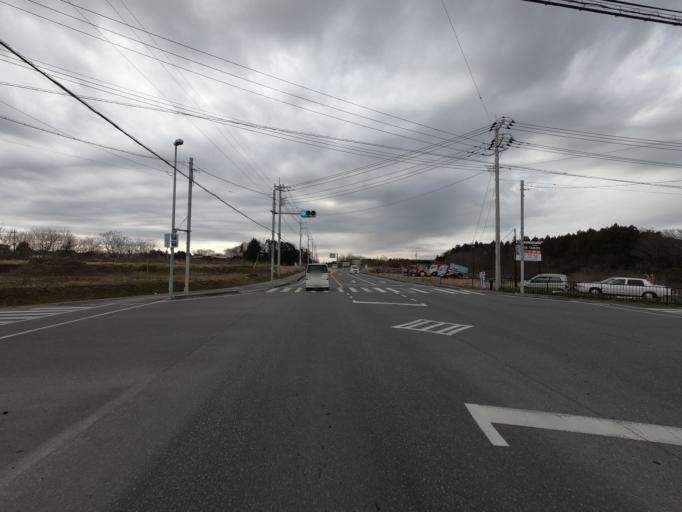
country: JP
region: Ibaraki
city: Ishioka
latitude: 36.0938
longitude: 140.3293
